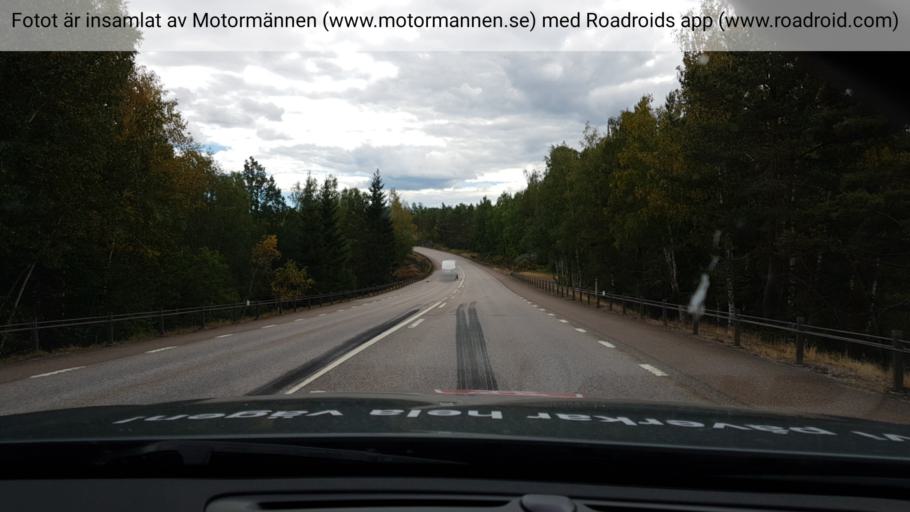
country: SE
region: Kalmar
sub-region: Oskarshamns Kommun
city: Oskarshamn
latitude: 57.5049
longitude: 16.5028
